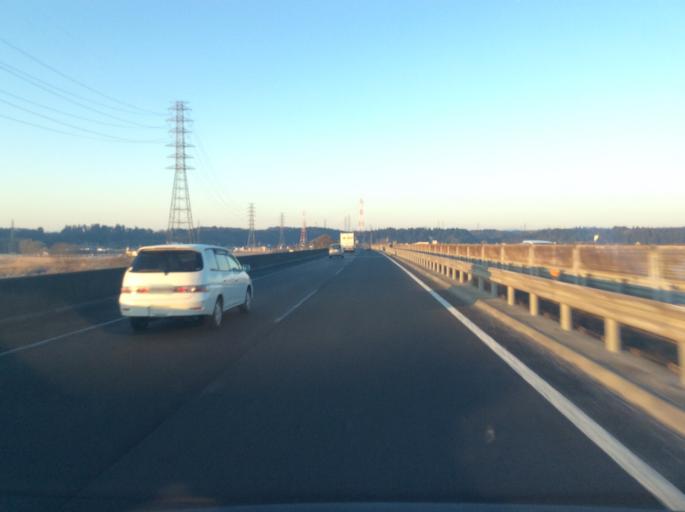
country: JP
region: Ibaraki
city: Mito-shi
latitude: 36.4218
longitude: 140.4321
